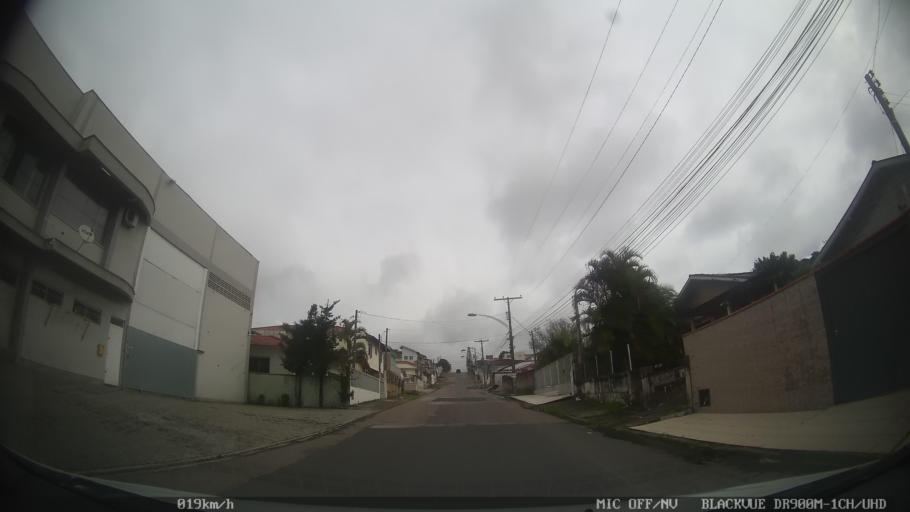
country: BR
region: Santa Catarina
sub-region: Biguacu
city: Biguacu
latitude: -27.5220
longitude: -48.6384
